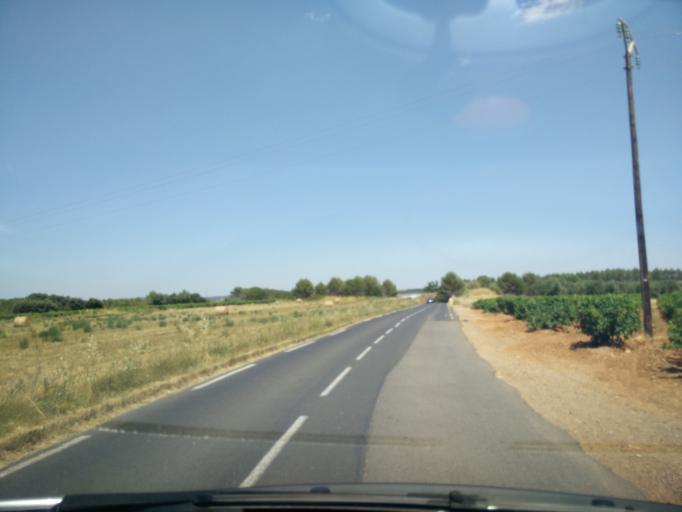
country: FR
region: Languedoc-Roussillon
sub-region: Departement de l'Herault
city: Saint-Christol
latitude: 43.7177
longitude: 4.1046
